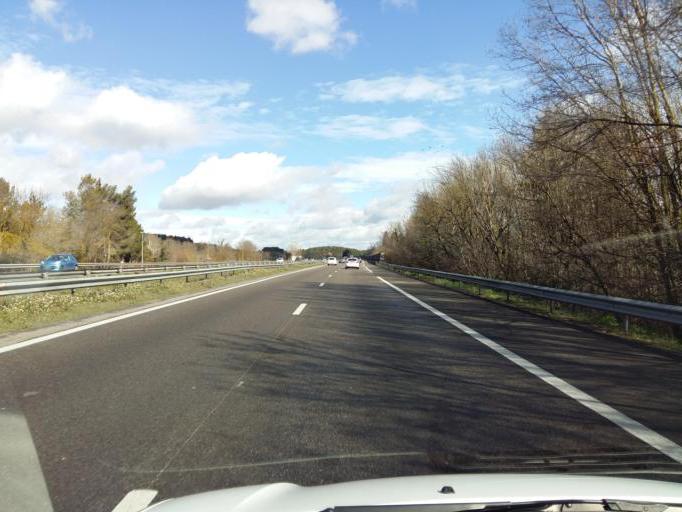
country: FR
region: Provence-Alpes-Cote d'Azur
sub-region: Departement des Bouches-du-Rhone
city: Bouc-Bel-Air
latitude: 43.4565
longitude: 5.4003
